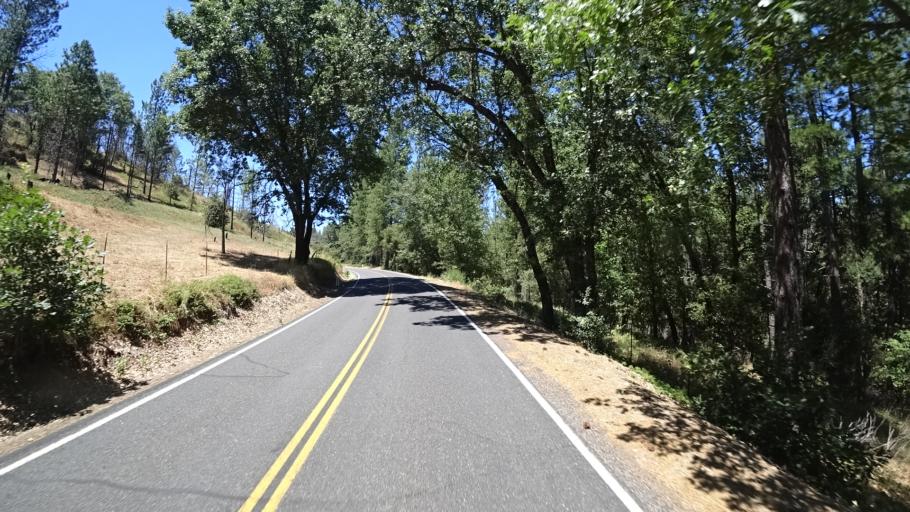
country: US
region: California
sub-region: Calaveras County
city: Mountain Ranch
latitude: 38.3050
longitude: -120.5062
